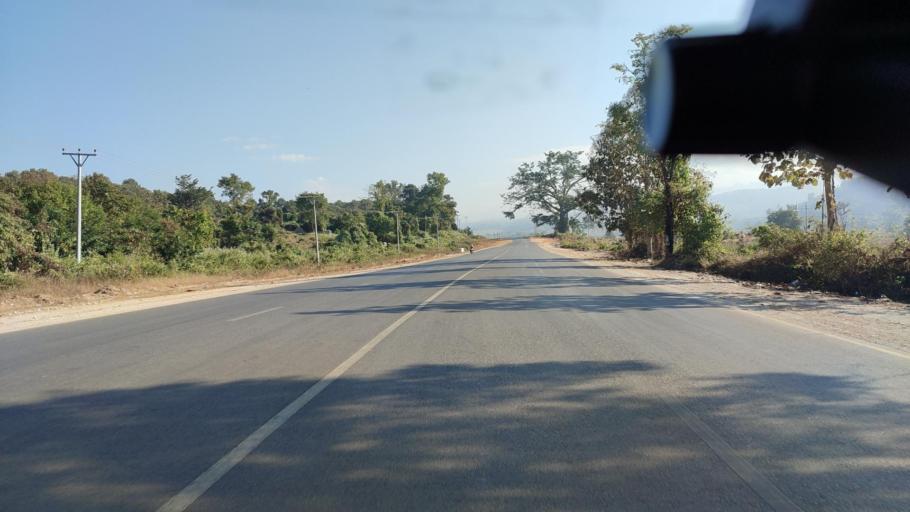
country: MM
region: Shan
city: Lashio
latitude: 23.1521
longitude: 97.8574
